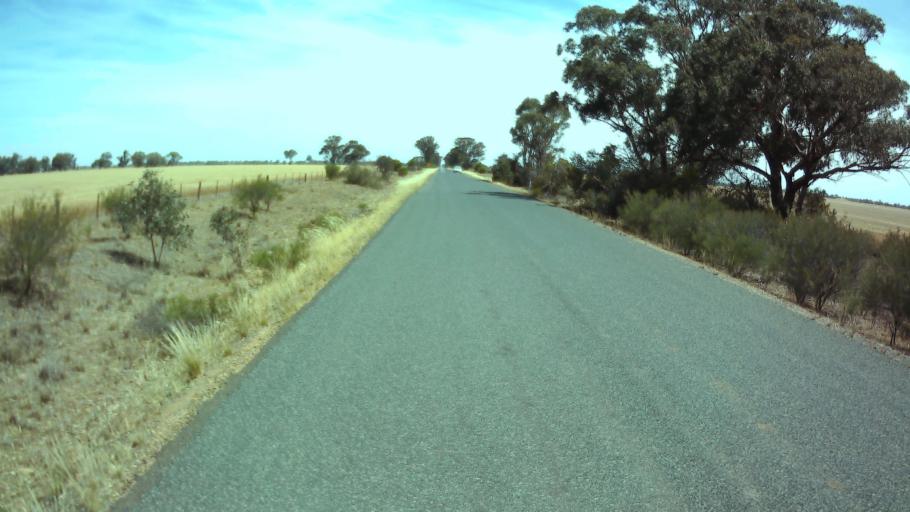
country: AU
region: New South Wales
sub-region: Weddin
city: Grenfell
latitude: -33.9650
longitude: 147.7810
